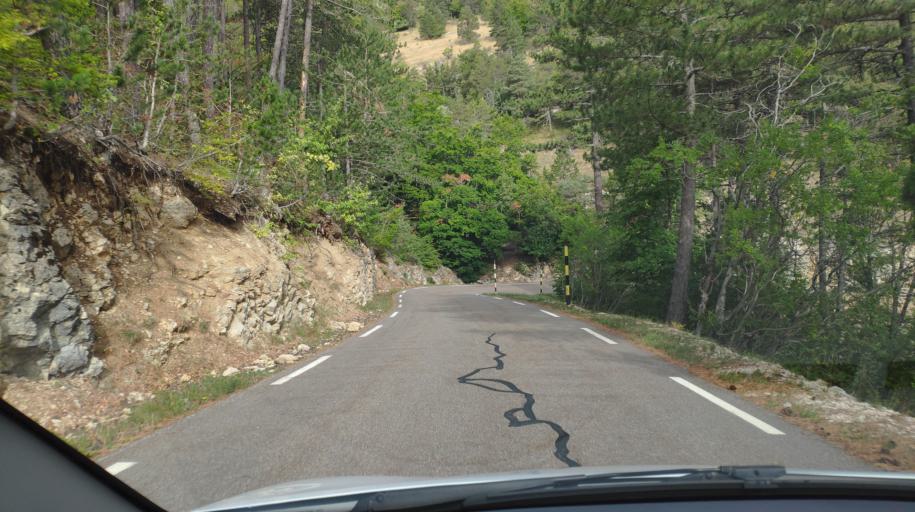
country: FR
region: Provence-Alpes-Cote d'Azur
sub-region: Departement du Vaucluse
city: Sault
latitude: 44.1546
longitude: 5.3451
